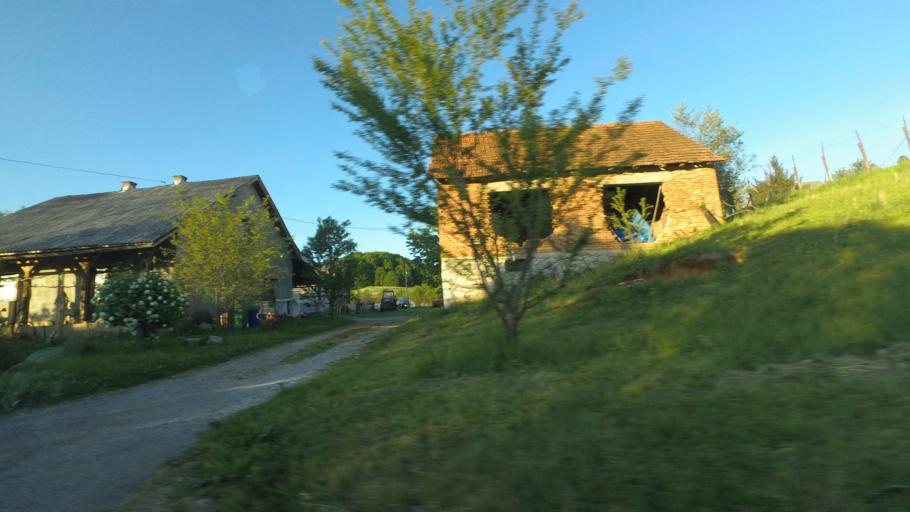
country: HR
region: Karlovacka
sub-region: Grad Karlovac
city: Karlovac
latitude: 45.4197
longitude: 15.5507
